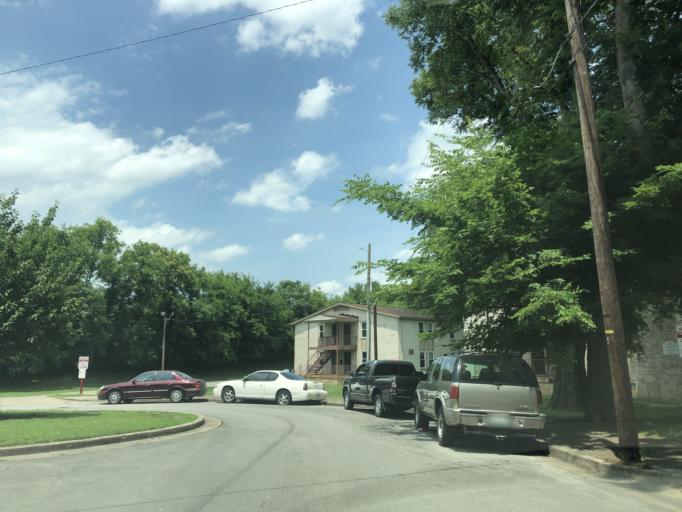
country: US
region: Tennessee
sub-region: Davidson County
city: Nashville
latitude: 36.1833
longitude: -86.7597
